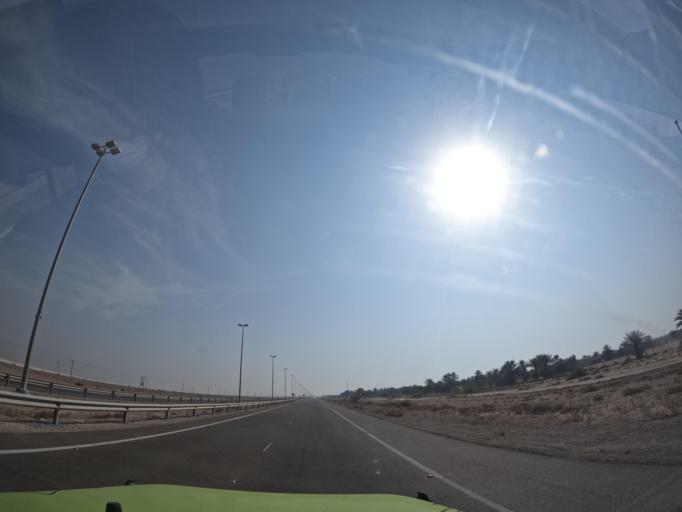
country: OM
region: Al Buraimi
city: Al Buraymi
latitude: 24.4871
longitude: 55.3948
